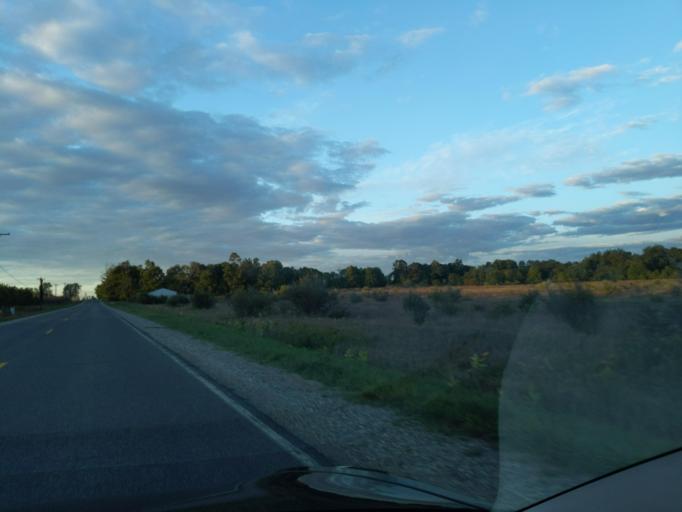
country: US
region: Michigan
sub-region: Antrim County
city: Elk Rapids
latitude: 44.8201
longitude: -85.4048
